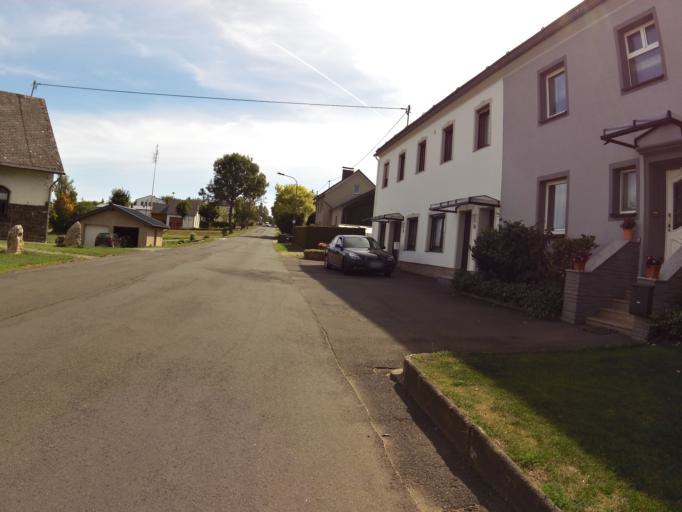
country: DE
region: Rheinland-Pfalz
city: Euscheid
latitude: 50.1276
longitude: 6.2673
